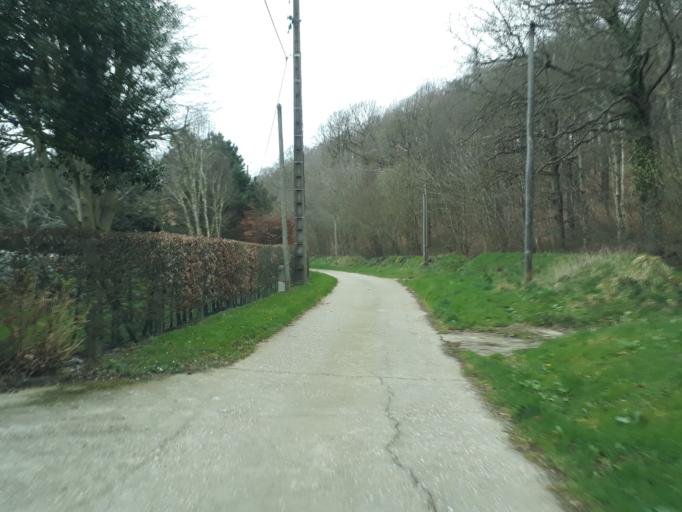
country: FR
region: Haute-Normandie
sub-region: Departement de la Seine-Maritime
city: Les Loges
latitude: 49.6710
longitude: 0.2700
